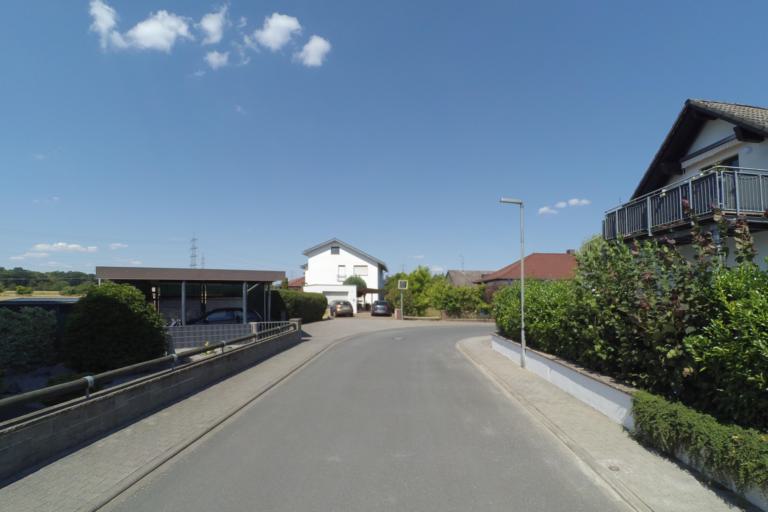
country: DE
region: Hesse
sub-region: Regierungsbezirk Darmstadt
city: Alsbach-Hahnlein
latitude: 49.7356
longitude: 8.5661
